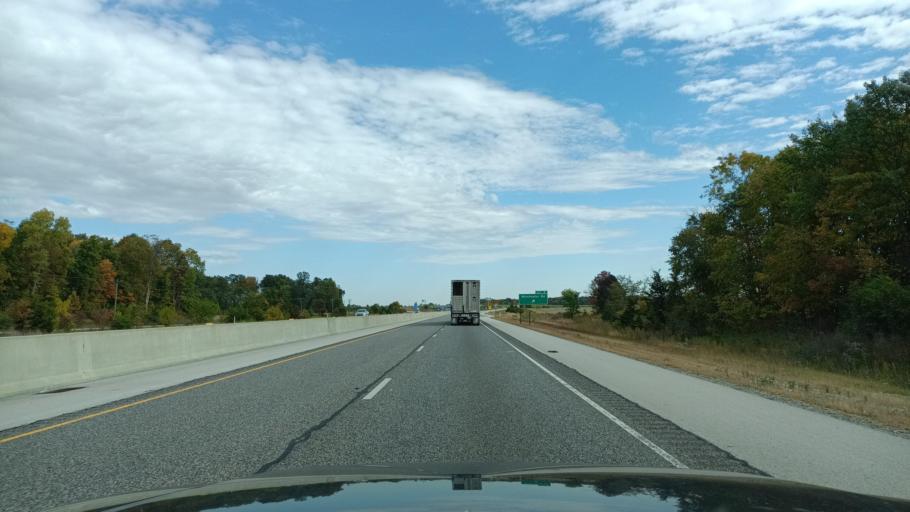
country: US
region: Indiana
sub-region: Wells County
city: Ossian
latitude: 40.9622
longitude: -85.1309
